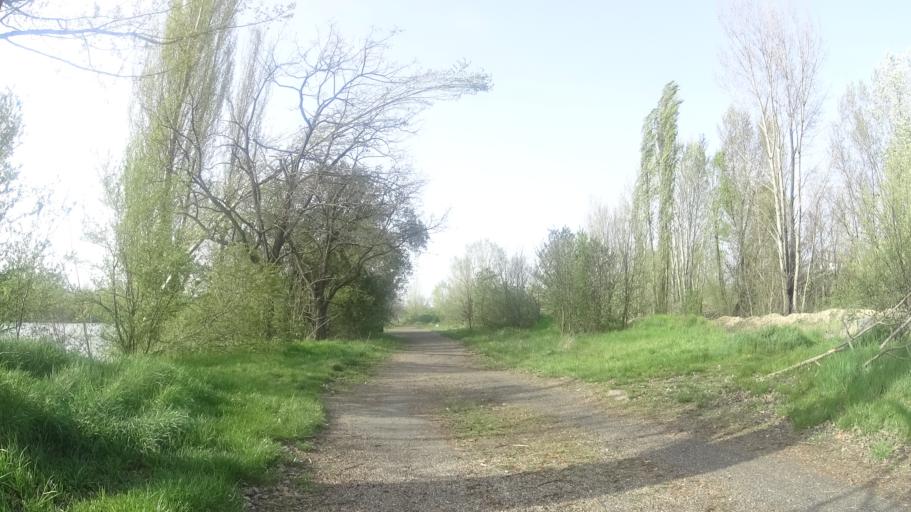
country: HU
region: Budapest
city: Budapest XX. keruelet
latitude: 47.4439
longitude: 19.0877
